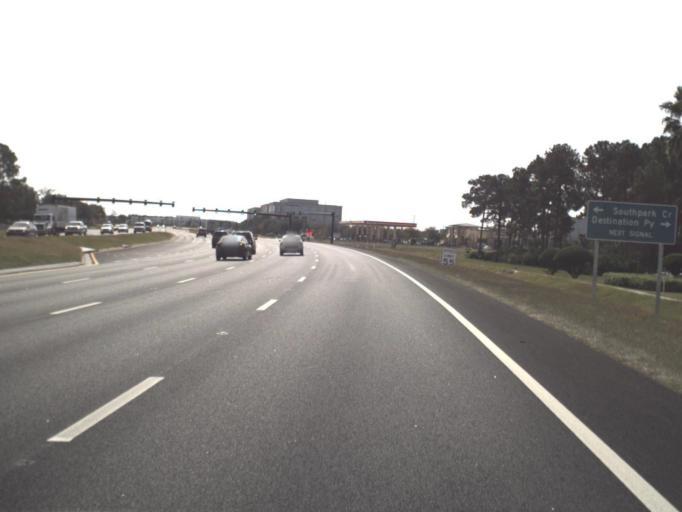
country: US
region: Florida
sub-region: Orange County
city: Tangelo Park
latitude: 28.4408
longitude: -81.4274
